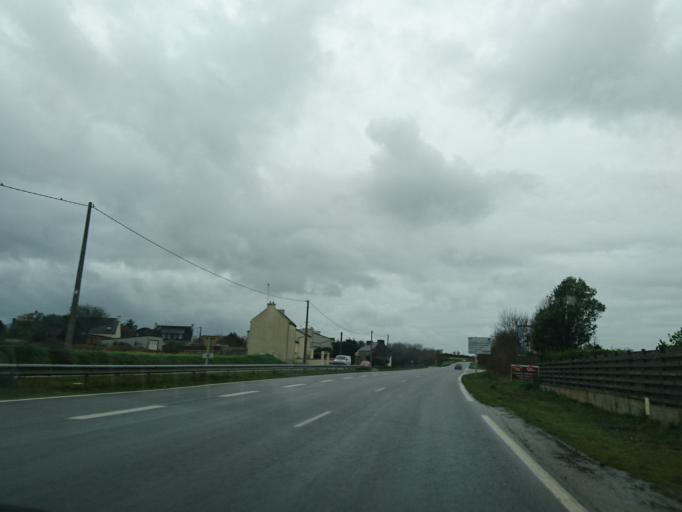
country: FR
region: Brittany
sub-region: Departement du Finistere
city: Plouzane
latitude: 48.3589
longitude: -4.6388
